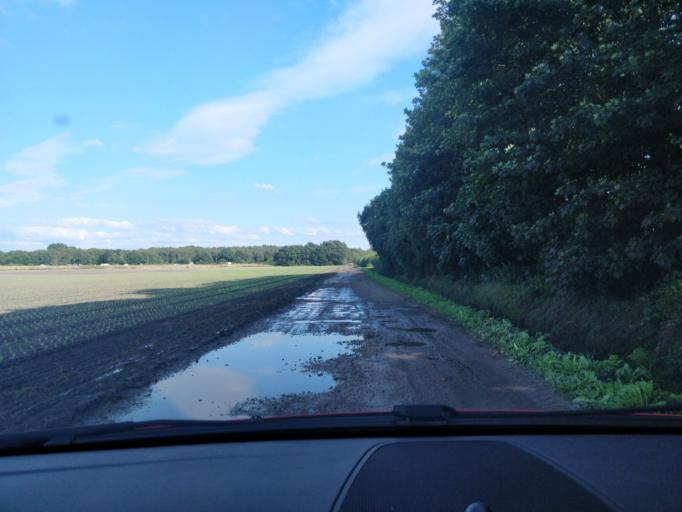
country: GB
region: England
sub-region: Lancashire
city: Banks
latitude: 53.6562
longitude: -2.9053
